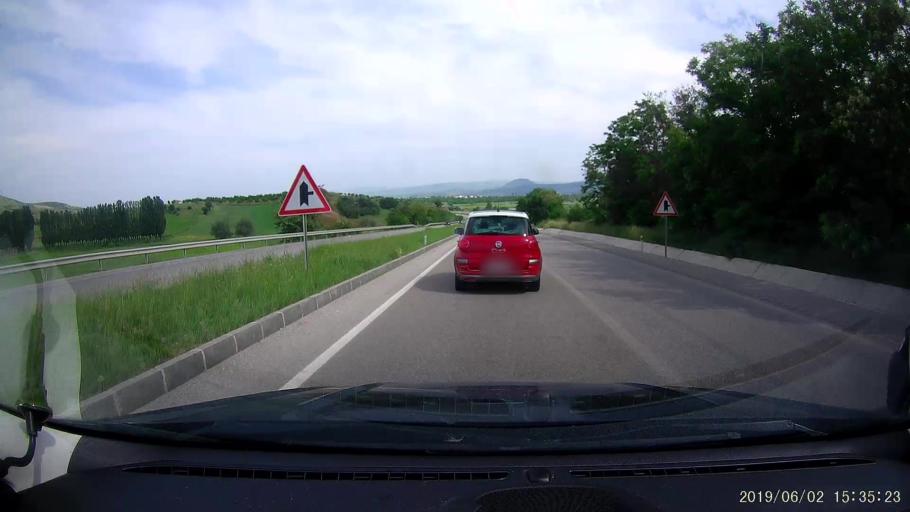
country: TR
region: Amasya
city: Gumushacikoy
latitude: 40.9014
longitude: 35.1826
